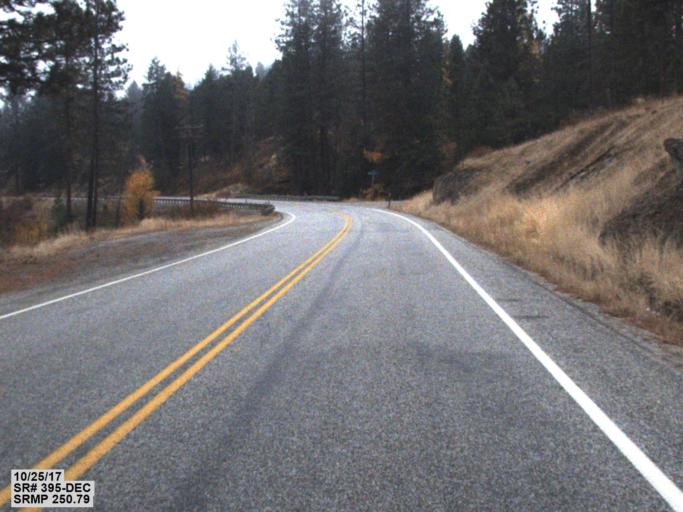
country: US
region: Washington
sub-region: Stevens County
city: Kettle Falls
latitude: 48.7480
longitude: -118.1351
